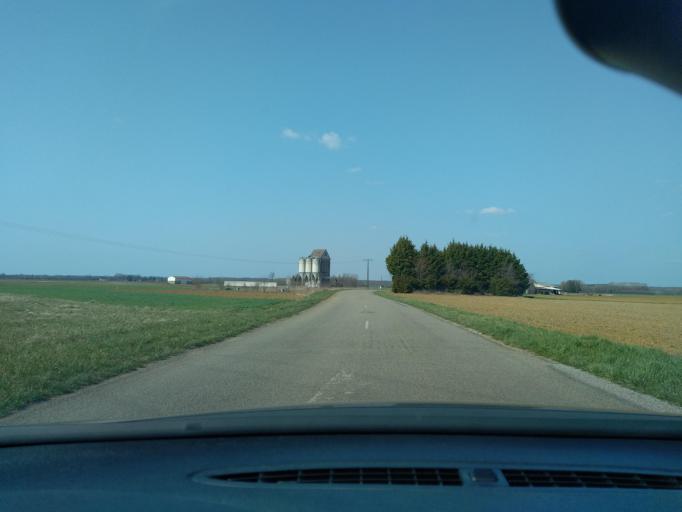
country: FR
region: Franche-Comte
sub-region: Departement du Jura
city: Mont-sous-Vaudrey
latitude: 46.9877
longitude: 5.6058
